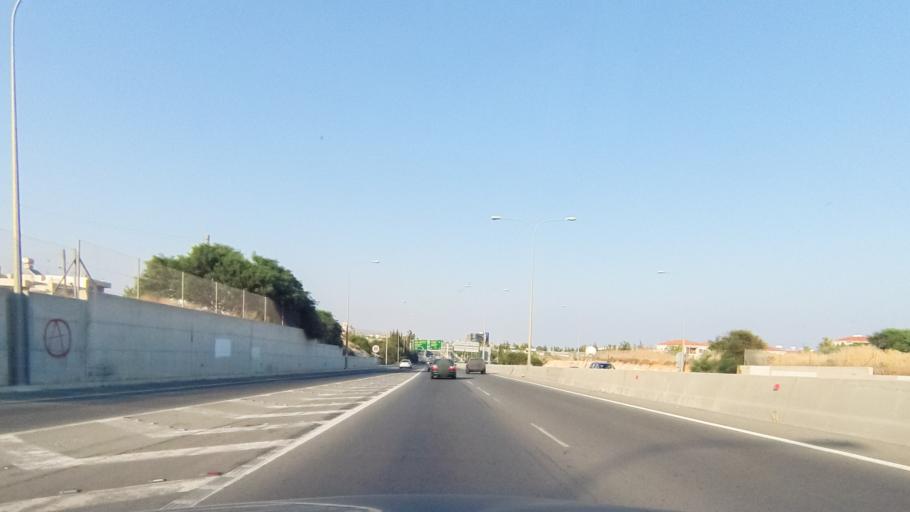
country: CY
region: Limassol
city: Limassol
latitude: 34.7058
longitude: 33.0519
